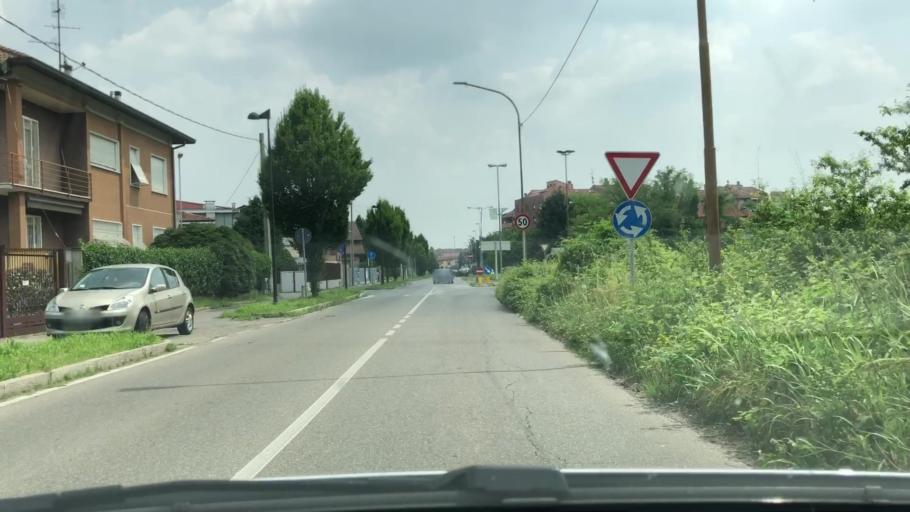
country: IT
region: Lombardy
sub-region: Provincia di Monza e Brianza
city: Desio
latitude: 45.6242
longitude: 9.1919
